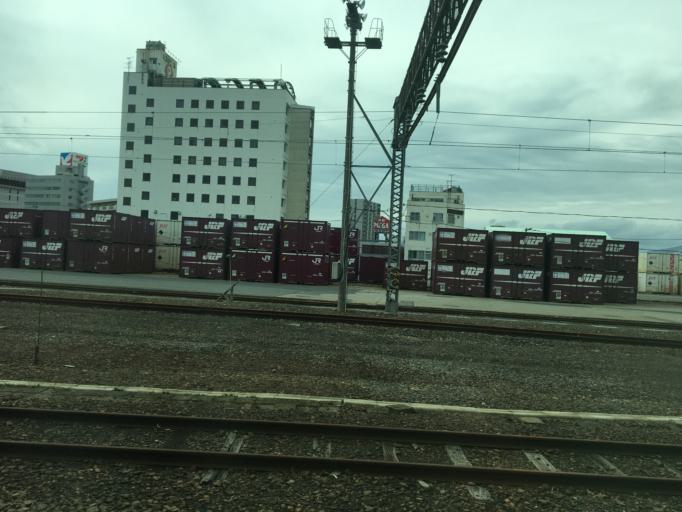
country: JP
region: Aomori
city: Hirosaki
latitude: 40.6023
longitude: 140.4842
